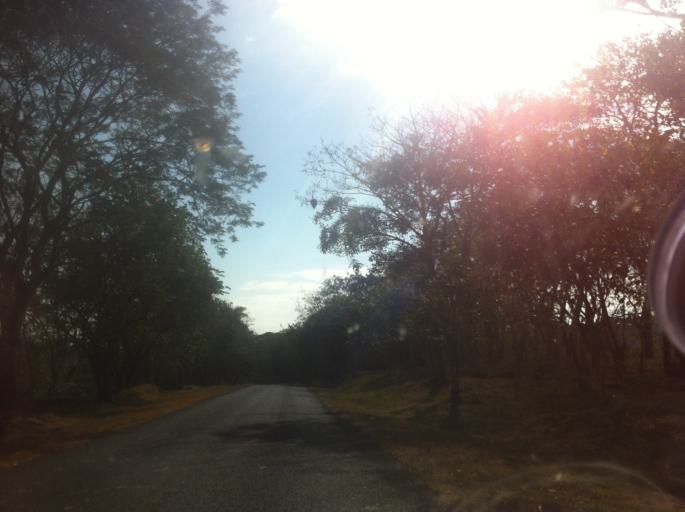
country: NI
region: Rio San Juan
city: San Miguelito
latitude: 11.4321
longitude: -84.8778
